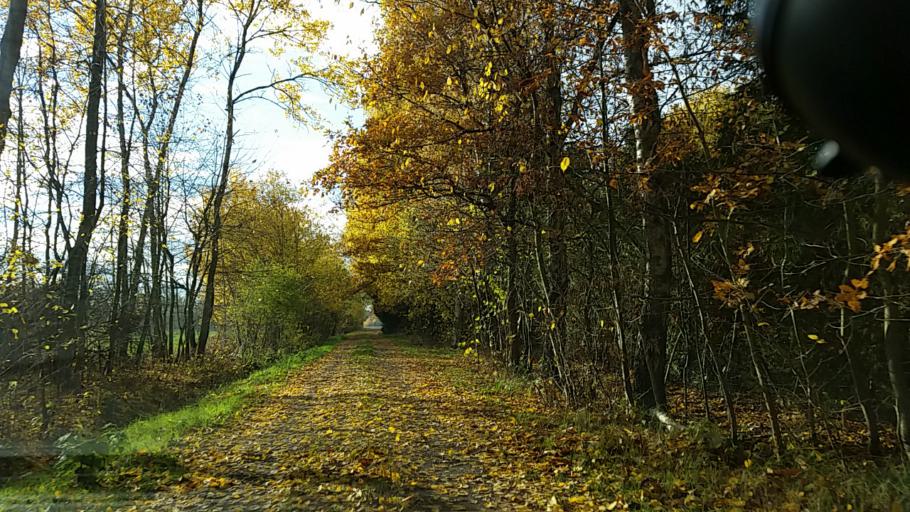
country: DE
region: Lower Saxony
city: Wolfsburg
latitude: 52.4560
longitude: 10.8307
